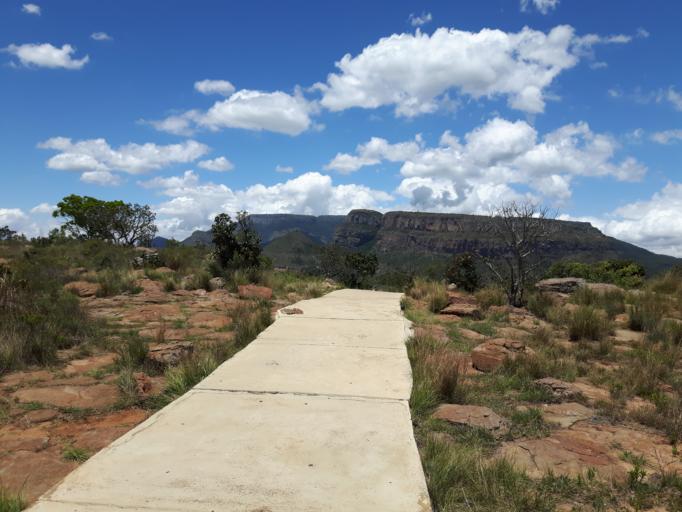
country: ZA
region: Limpopo
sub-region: Mopani District Municipality
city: Hoedspruit
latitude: -24.5737
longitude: 30.7986
